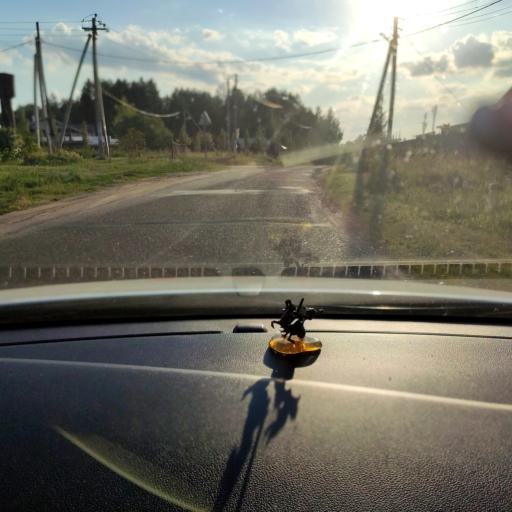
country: RU
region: Tatarstan
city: Pestretsy
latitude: 55.6157
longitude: 49.4920
